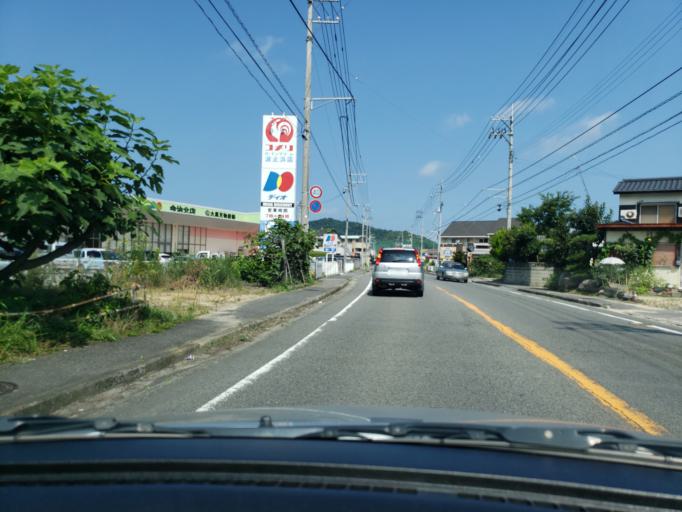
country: JP
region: Ehime
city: Hojo
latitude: 34.0985
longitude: 132.9717
